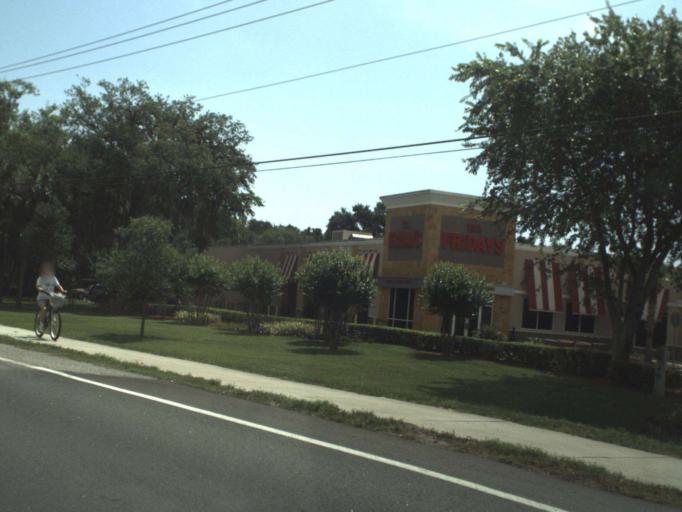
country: US
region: Florida
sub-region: Volusia County
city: Port Orange
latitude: 29.1282
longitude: -81.0040
